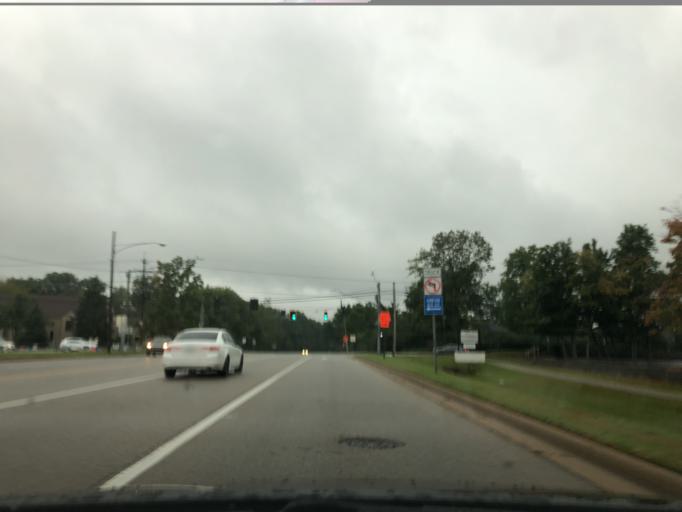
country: US
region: Ohio
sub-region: Hamilton County
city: Blue Ash
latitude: 39.2386
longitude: -84.3911
